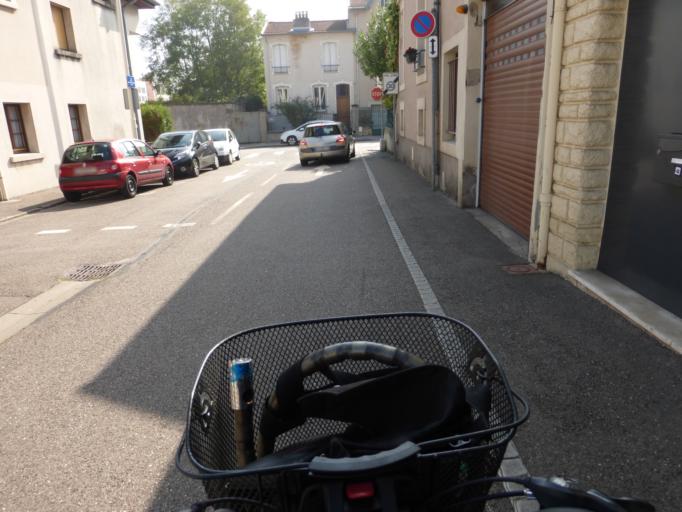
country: FR
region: Lorraine
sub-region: Departement de Meurthe-et-Moselle
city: Villers-les-Nancy
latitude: 48.6744
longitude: 6.1671
